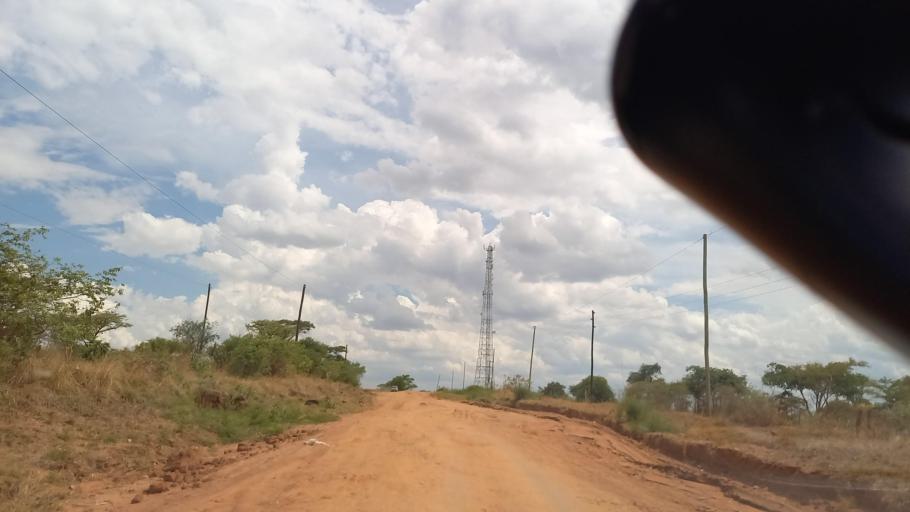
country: ZM
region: Southern
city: Nakambala
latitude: -16.0343
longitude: 27.9700
